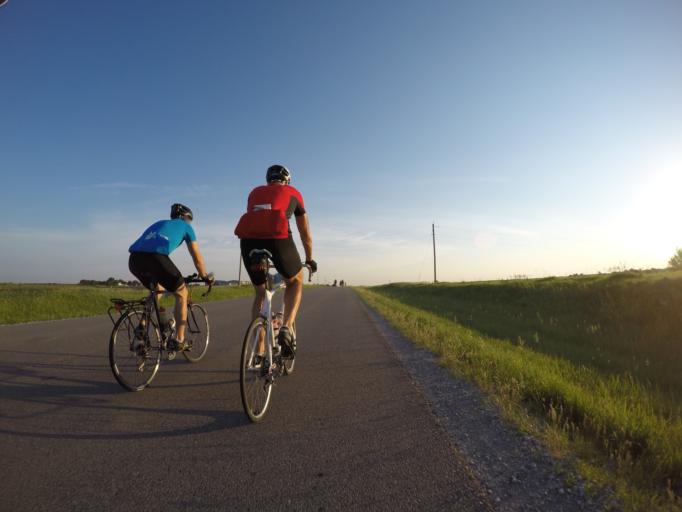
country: US
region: Kansas
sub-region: Marshall County
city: Marysville
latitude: 39.8531
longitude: -96.6009
